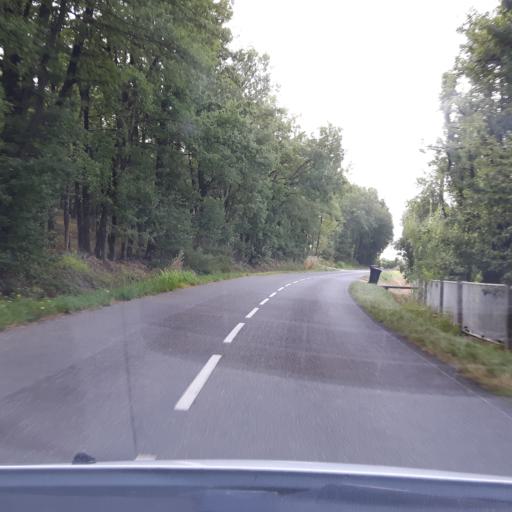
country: FR
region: Midi-Pyrenees
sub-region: Departement de la Haute-Garonne
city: Bouloc
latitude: 43.7952
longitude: 1.4135
